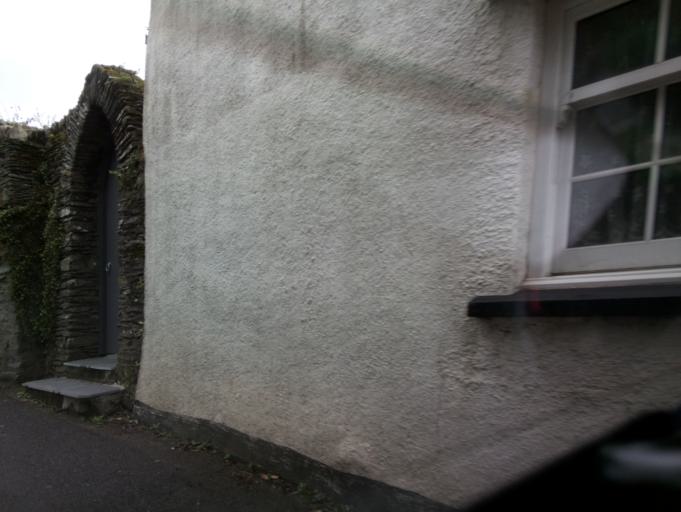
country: GB
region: England
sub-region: Devon
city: Dartmouth
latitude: 50.3249
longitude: -3.5988
